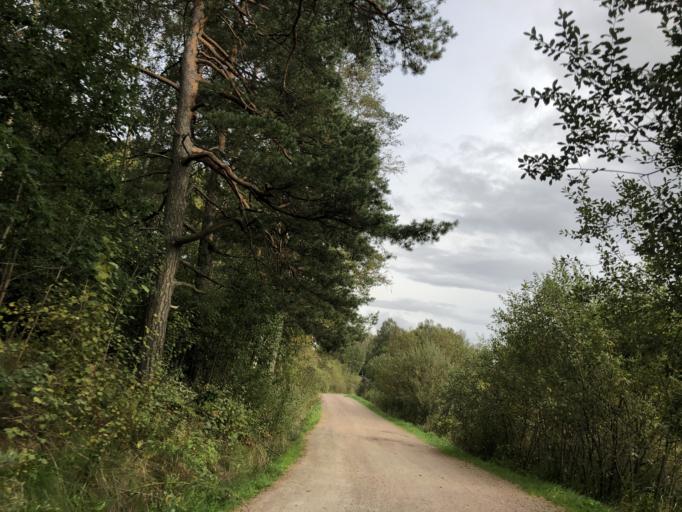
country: SE
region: Vaestra Goetaland
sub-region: Goteborg
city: Majorna
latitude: 57.7424
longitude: 11.9005
